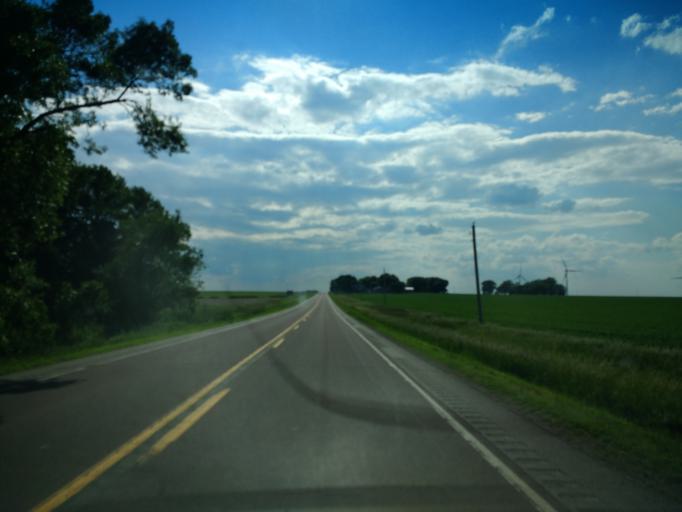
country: US
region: Iowa
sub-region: O'Brien County
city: Hartley
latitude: 43.1838
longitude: -95.3397
